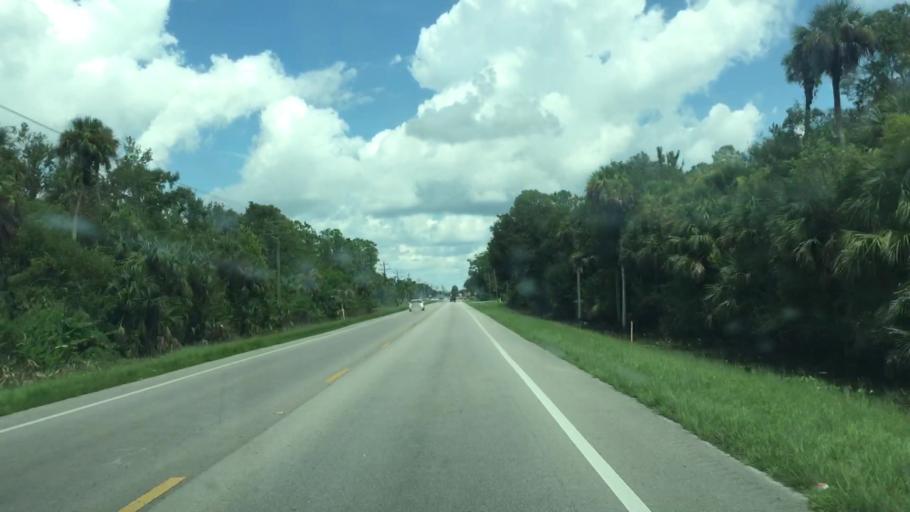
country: US
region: Florida
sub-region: Collier County
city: Immokalee
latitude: 26.4053
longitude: -81.4171
